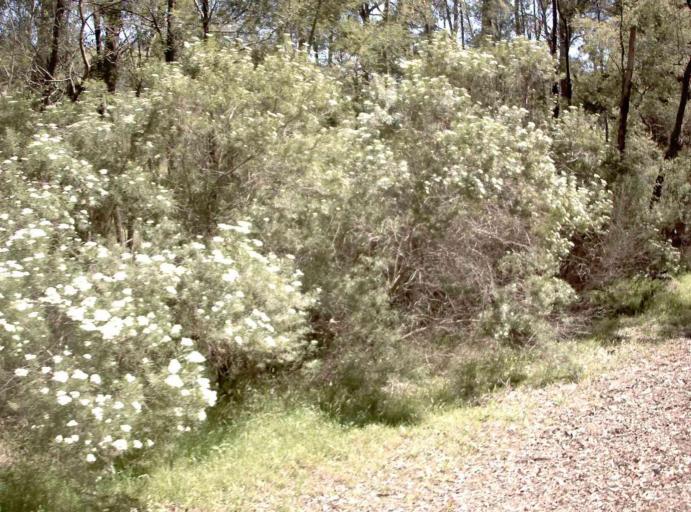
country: AU
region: Victoria
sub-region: East Gippsland
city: Lakes Entrance
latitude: -37.3577
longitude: 148.2268
